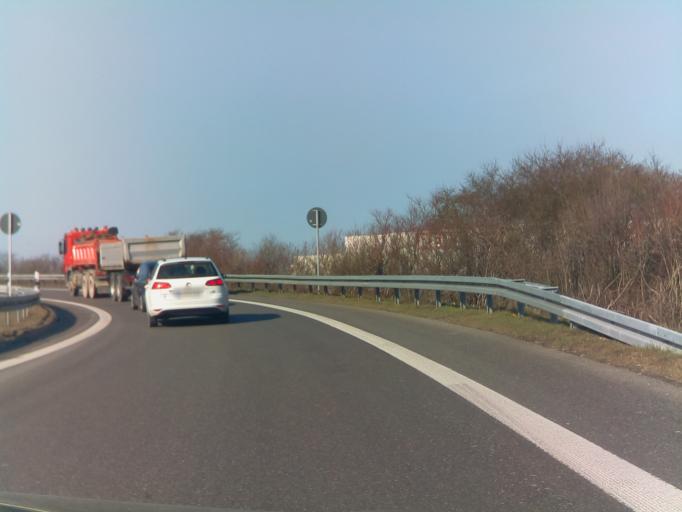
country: DE
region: Baden-Wuerttemberg
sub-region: Regierungsbezirk Stuttgart
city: Bondorf
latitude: 48.5042
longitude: 8.8425
